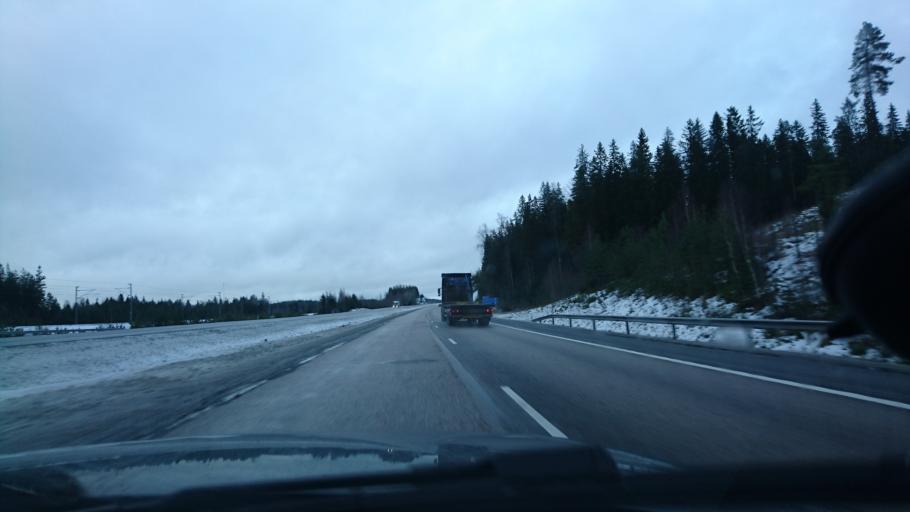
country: FI
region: Uusimaa
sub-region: Porvoo
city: Pukkila
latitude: 60.7636
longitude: 25.4650
